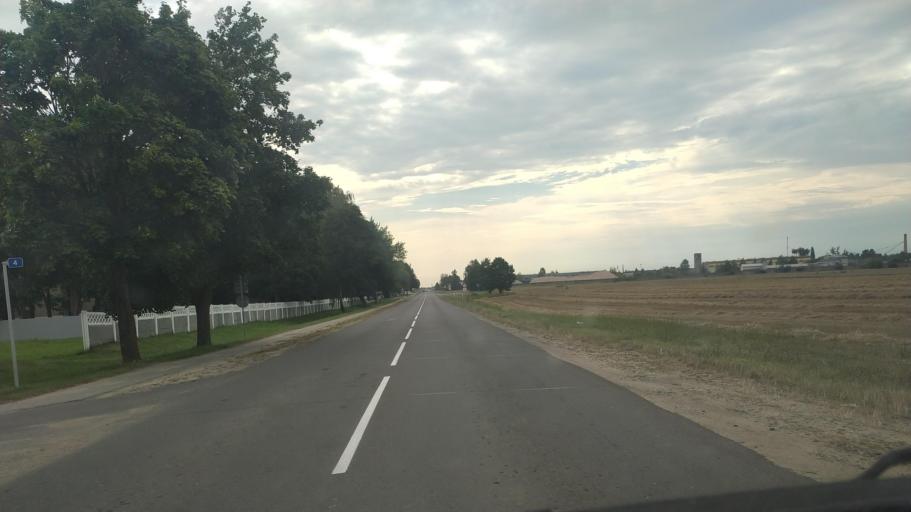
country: BY
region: Brest
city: Byaroza
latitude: 52.5552
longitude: 24.9222
